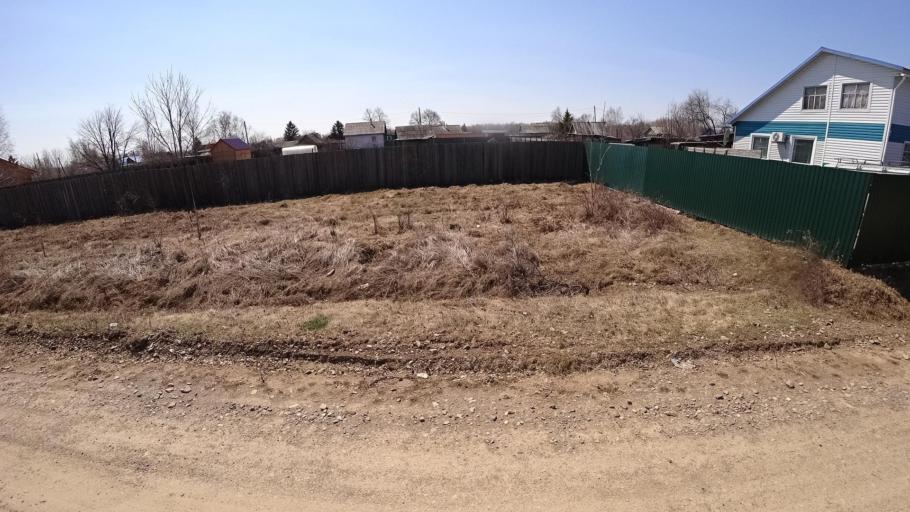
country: RU
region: Khabarovsk Krai
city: Khurba
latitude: 50.4119
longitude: 136.8675
